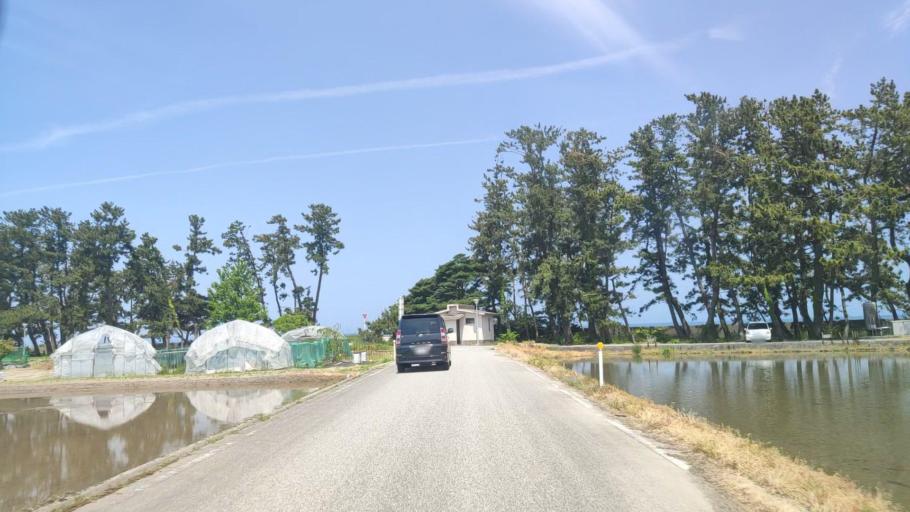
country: JP
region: Toyama
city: Nyuzen
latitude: 36.9622
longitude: 137.5669
